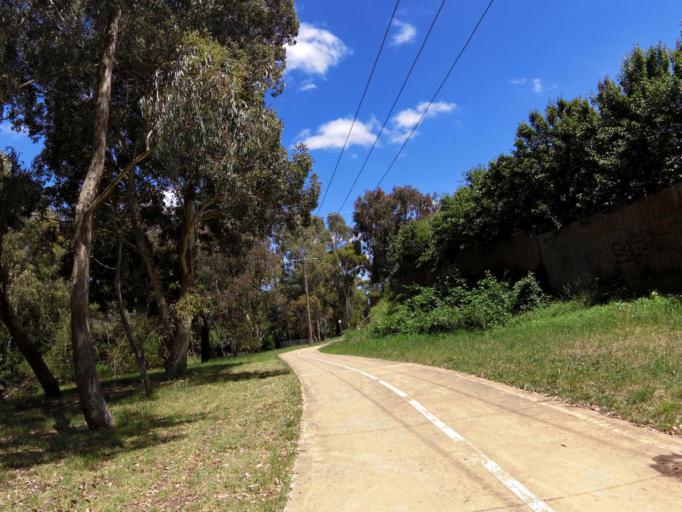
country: AU
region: Victoria
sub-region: Moreland
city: Fawkner
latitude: -37.7212
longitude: 144.9719
